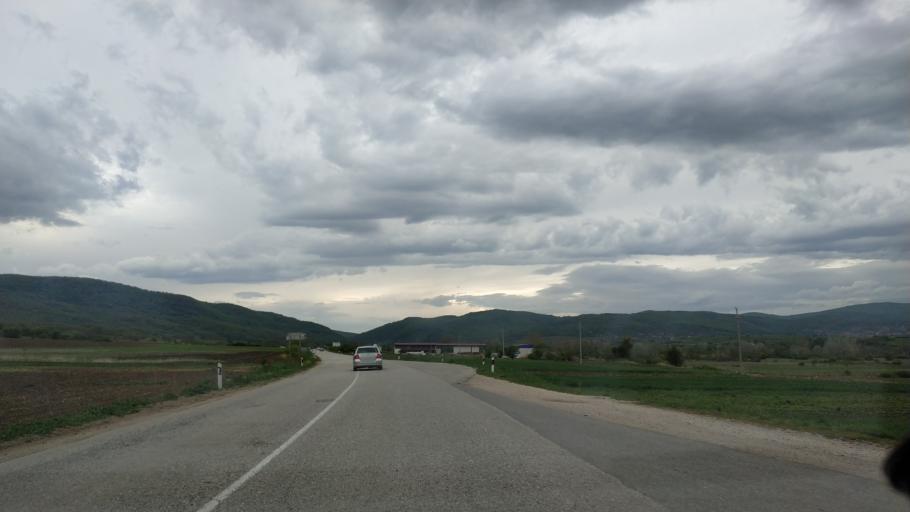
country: RS
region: Central Serbia
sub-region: Zajecarski Okrug
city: Soko Banja
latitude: 43.6567
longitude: 21.8034
